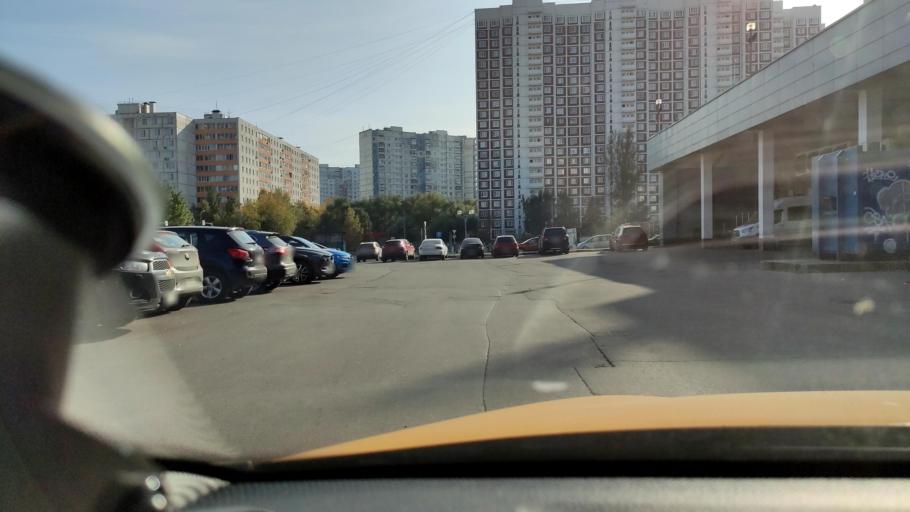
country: RU
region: Moscow
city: Altuf'yevskiy
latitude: 55.8884
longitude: 37.5899
